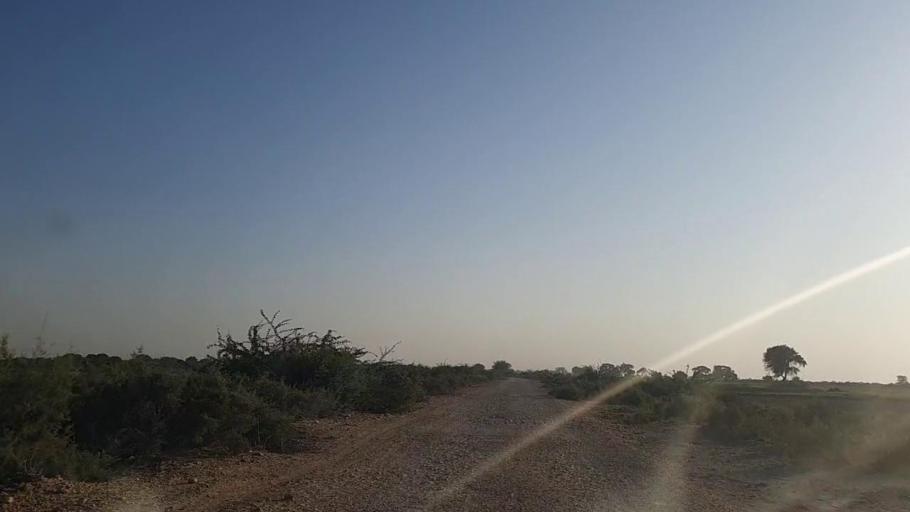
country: PK
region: Sindh
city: Jati
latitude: 24.4355
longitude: 68.1920
